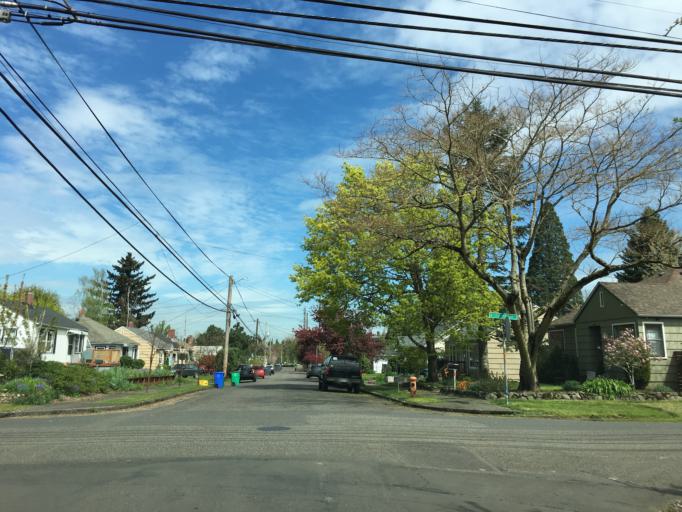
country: US
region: Oregon
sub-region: Multnomah County
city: Lents
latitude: 45.5314
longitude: -122.5820
